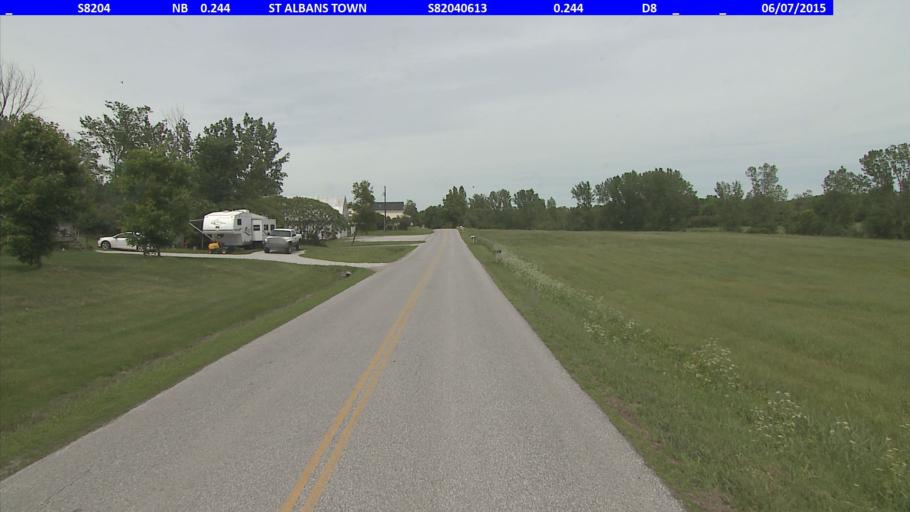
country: US
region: Vermont
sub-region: Franklin County
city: Saint Albans
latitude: 44.8063
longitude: -73.1116
